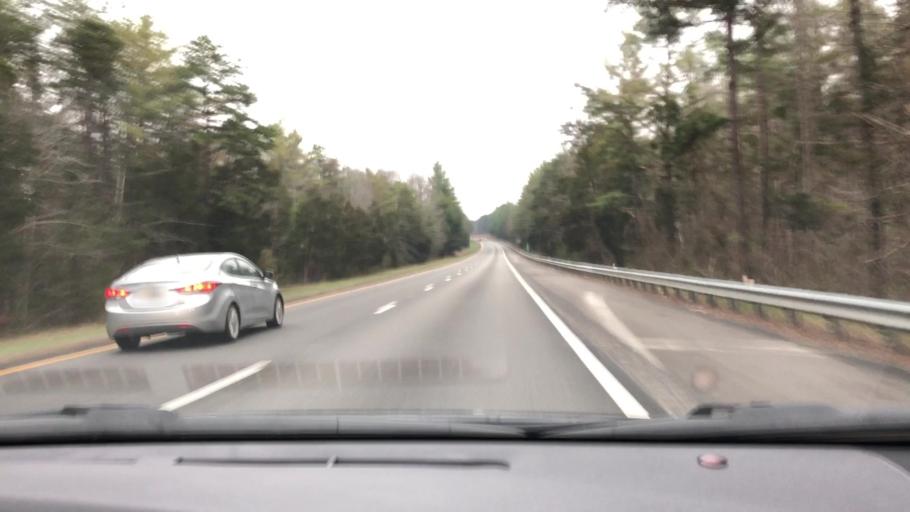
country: US
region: Virginia
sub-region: Fluvanna County
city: Palmyra
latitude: 37.9638
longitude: -78.1817
